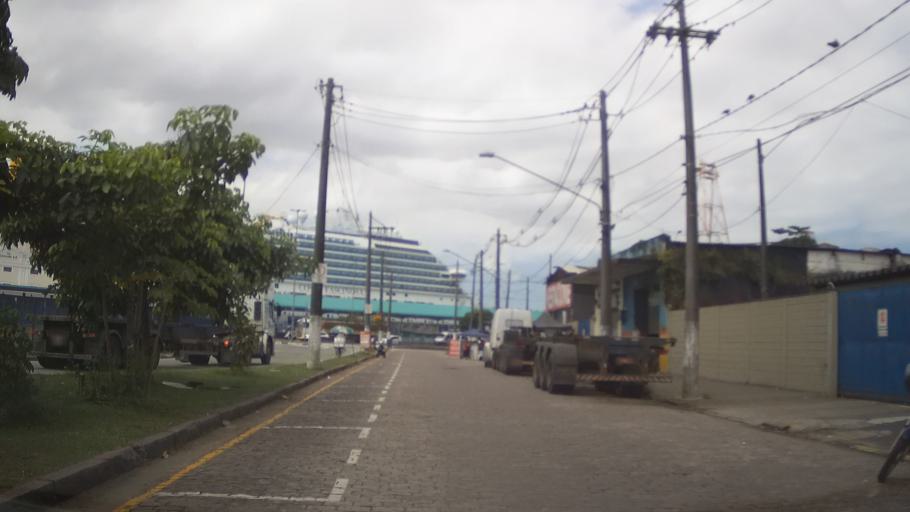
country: BR
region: Sao Paulo
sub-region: Santos
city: Santos
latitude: -23.9510
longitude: -46.3127
